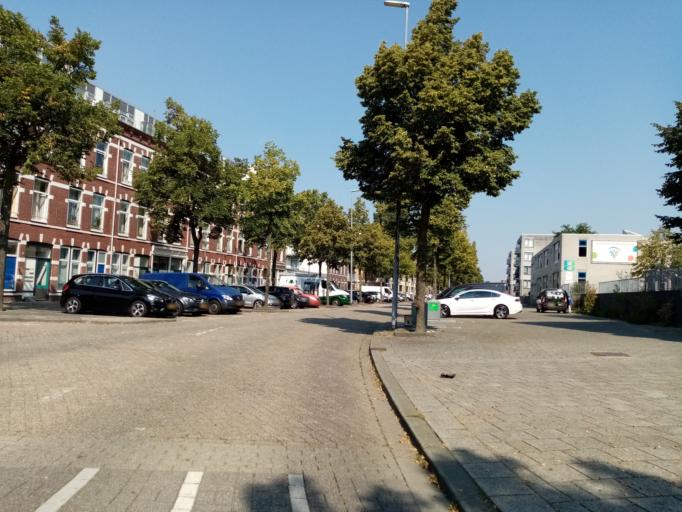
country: NL
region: South Holland
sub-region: Gemeente Rotterdam
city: Rotterdam
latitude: 51.9117
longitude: 4.5058
